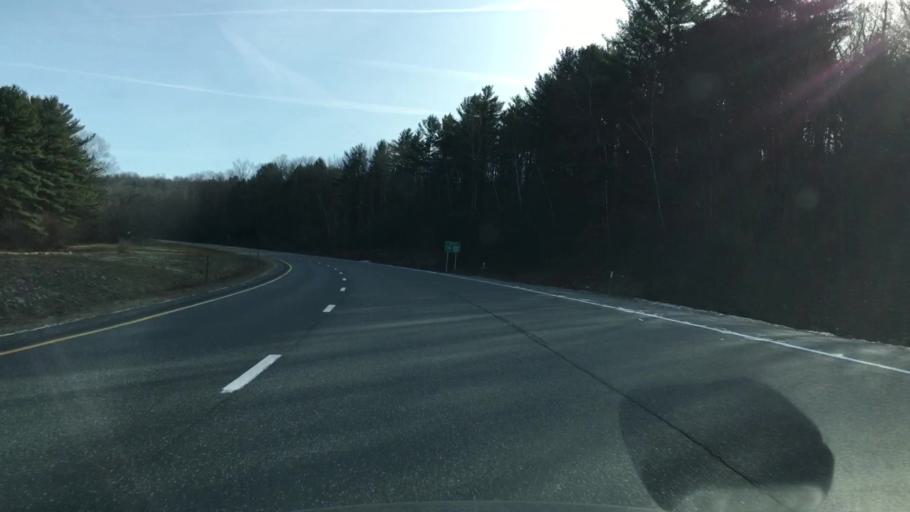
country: US
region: New Hampshire
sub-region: Grafton County
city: Lebanon
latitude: 43.6299
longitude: -72.2105
